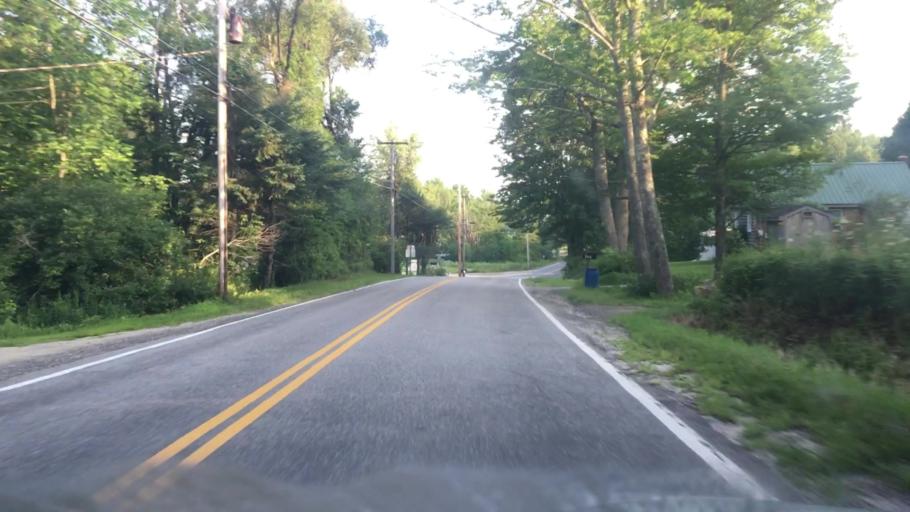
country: US
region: Maine
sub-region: Cumberland County
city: Freeport
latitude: 43.9179
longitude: -70.0904
